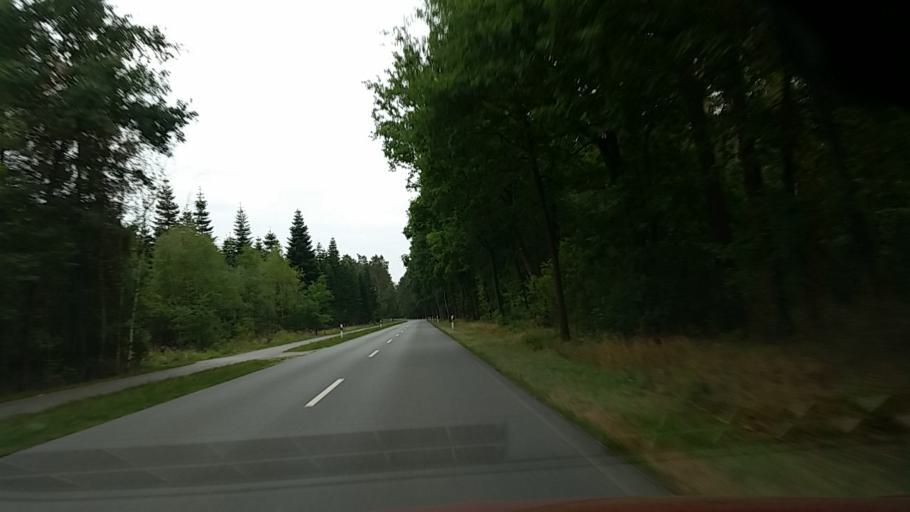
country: DE
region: Lower Saxony
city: Bokensdorf
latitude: 52.5313
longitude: 10.7167
